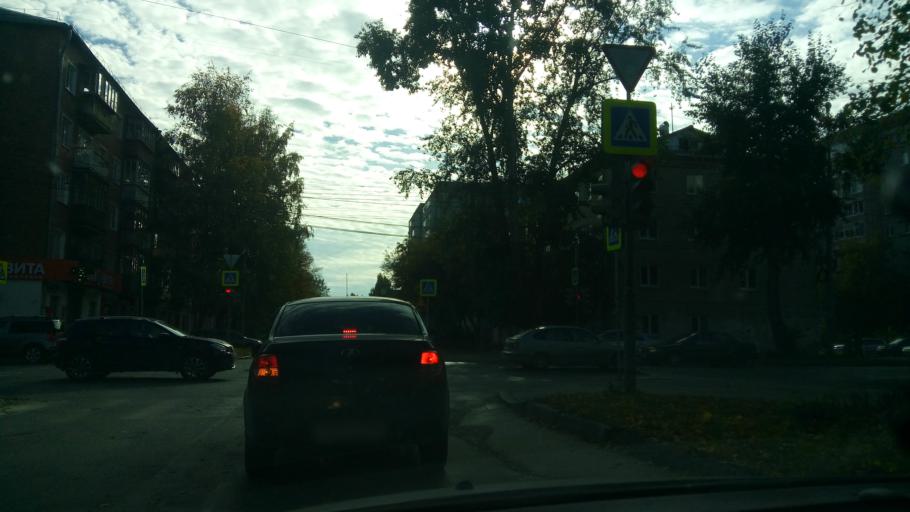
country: RU
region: Sverdlovsk
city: Yekaterinburg
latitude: 56.9030
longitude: 60.6034
